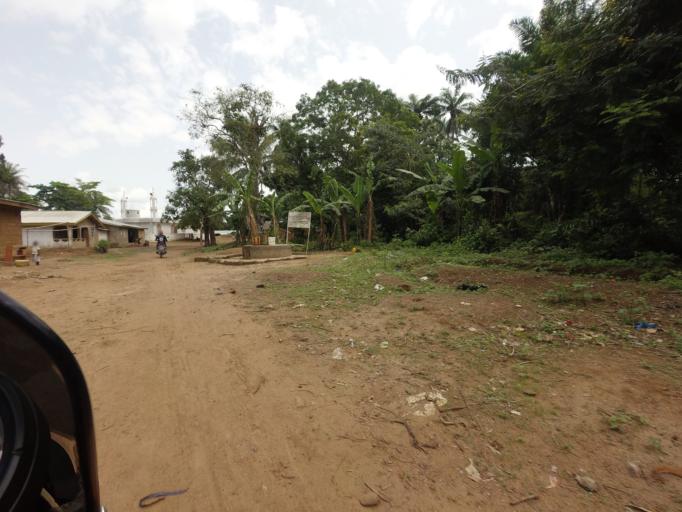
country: SL
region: Northern Province
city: Kambia
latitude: 9.0536
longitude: -12.9922
